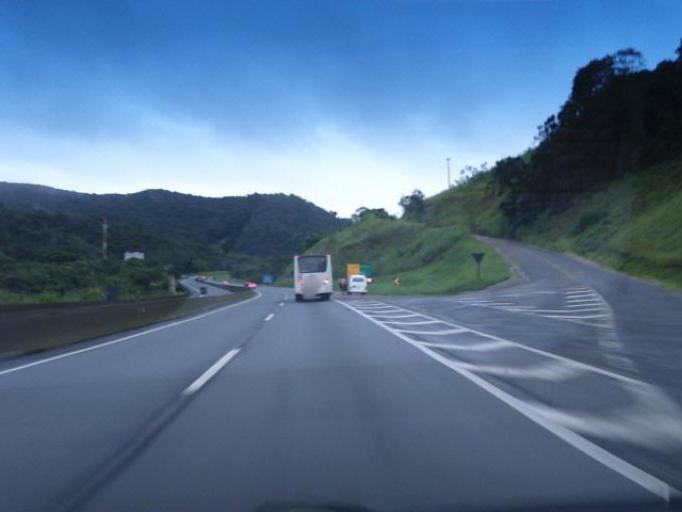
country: BR
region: Sao Paulo
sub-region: Miracatu
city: Miracatu
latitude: -24.1462
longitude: -47.2935
